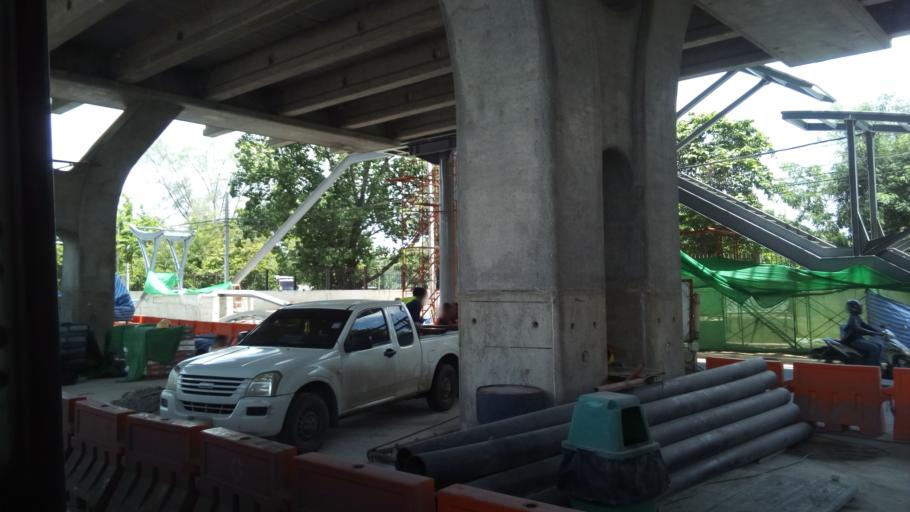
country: TH
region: Bangkok
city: Don Mueang
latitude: 13.9103
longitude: 100.6172
